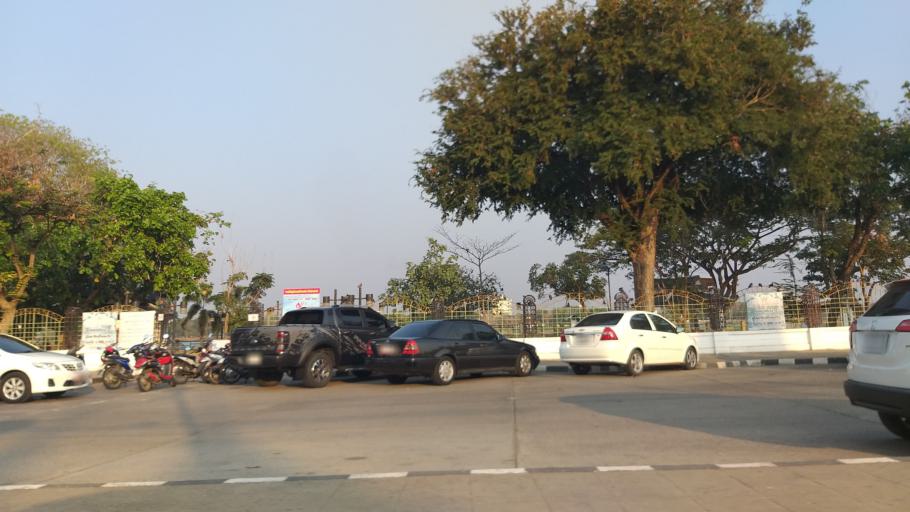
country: TH
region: Khon Kaen
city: Khon Kaen
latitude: 16.4143
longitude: 102.8353
